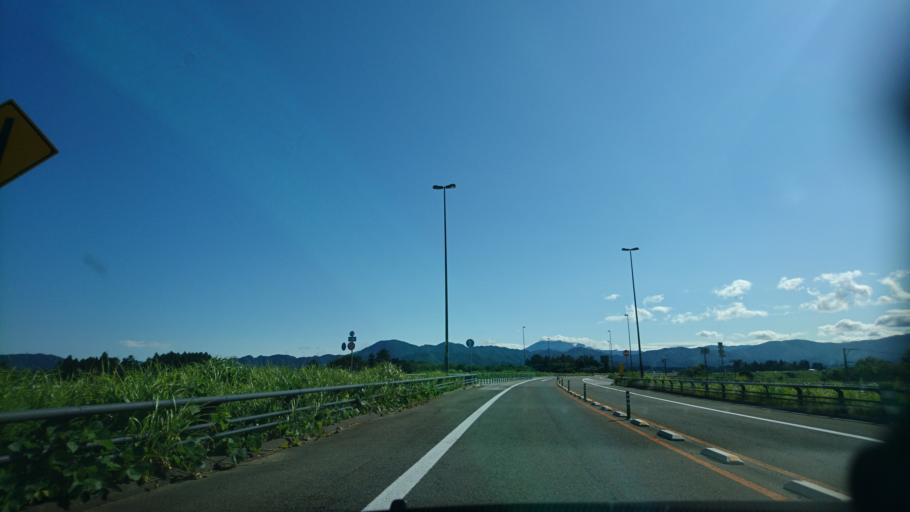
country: JP
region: Akita
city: Kakunodatemachi
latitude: 39.6097
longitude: 140.5579
